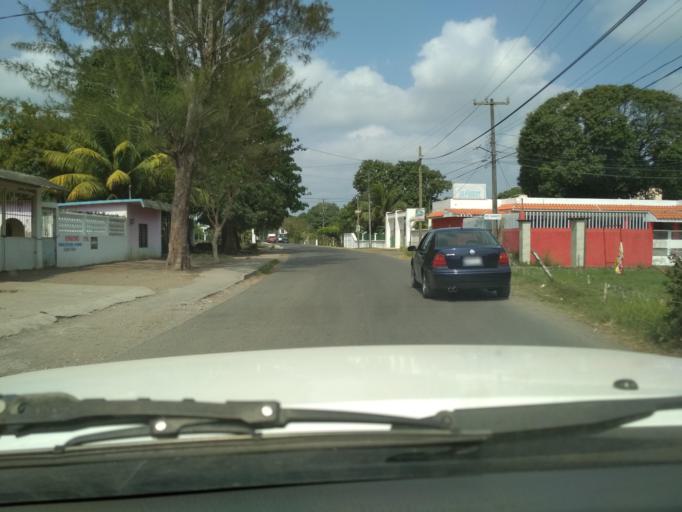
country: MX
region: Veracruz
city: El Tejar
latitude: 19.0764
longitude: -96.1670
